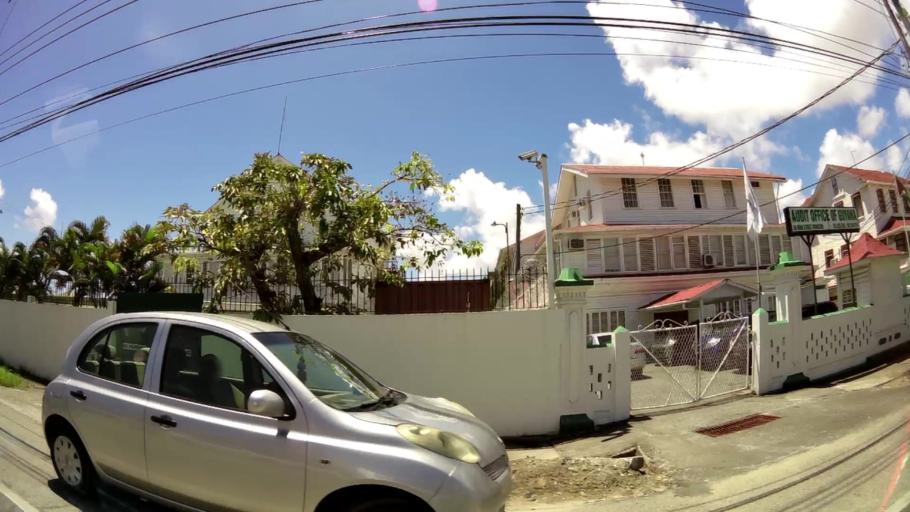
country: GY
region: Demerara-Mahaica
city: Georgetown
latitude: 6.8236
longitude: -58.1624
